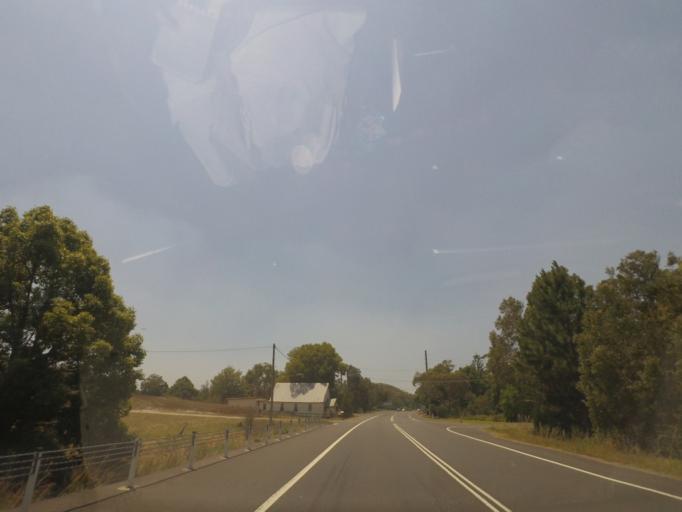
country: AU
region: New South Wales
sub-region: Port Stephens Shire
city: Medowie
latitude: -32.8070
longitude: 151.8607
